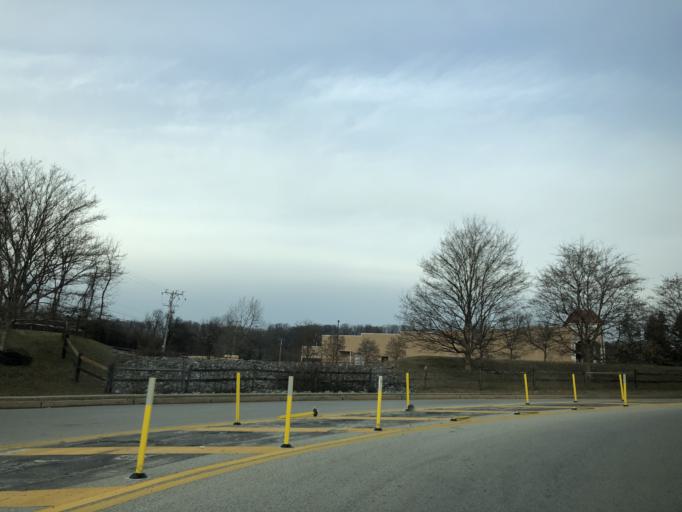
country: US
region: Pennsylvania
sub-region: Chester County
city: Downingtown
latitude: 40.0157
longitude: -75.6864
